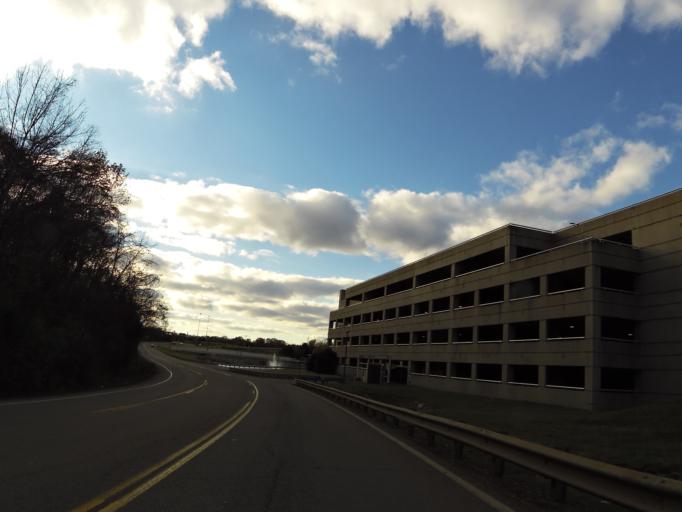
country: US
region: Tennessee
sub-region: Knox County
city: Knoxville
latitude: 35.9379
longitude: -83.9421
